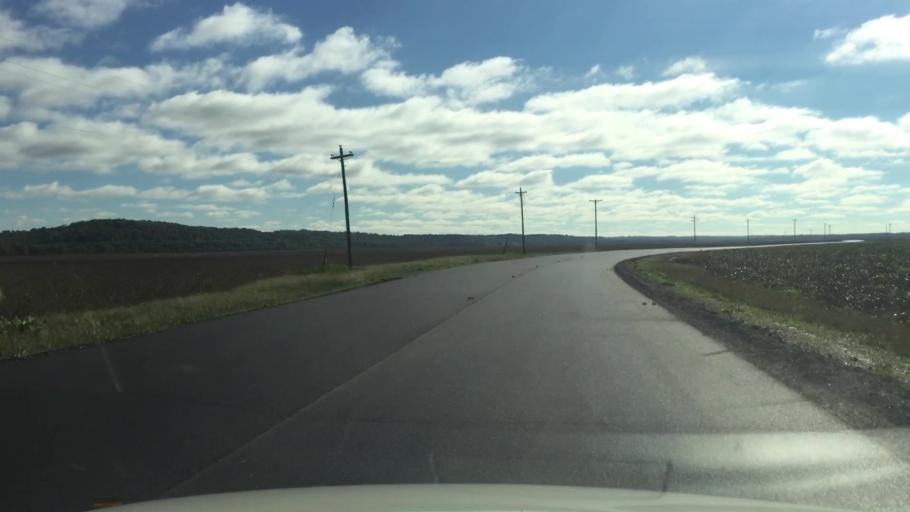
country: US
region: Missouri
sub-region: Howard County
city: New Franklin
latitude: 39.0001
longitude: -92.6760
